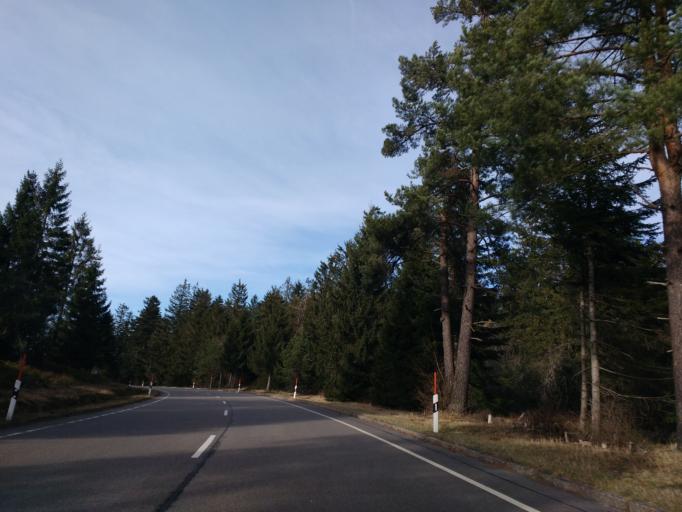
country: DE
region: Baden-Wuerttemberg
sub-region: Freiburg Region
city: Bad Peterstal-Griesbach
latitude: 48.4999
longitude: 8.2350
